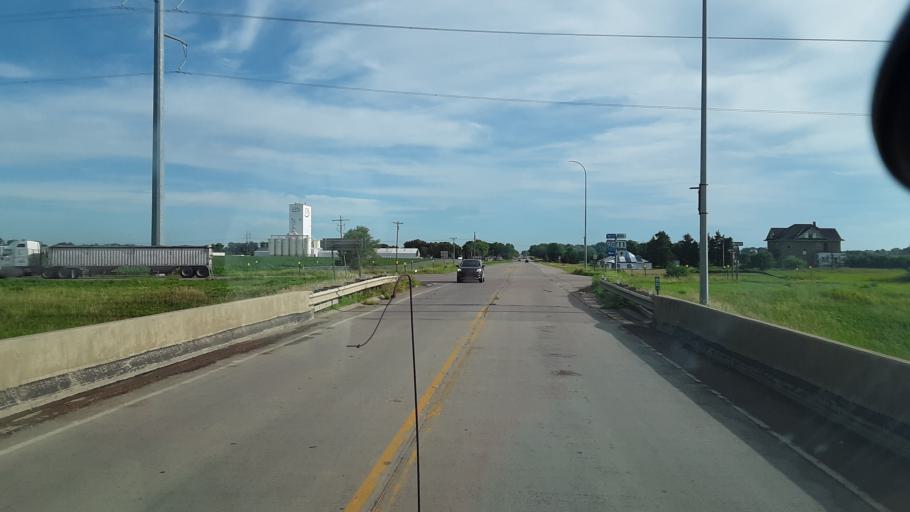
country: US
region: South Dakota
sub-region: Minnehaha County
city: Brandon
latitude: 43.6086
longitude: -96.5722
